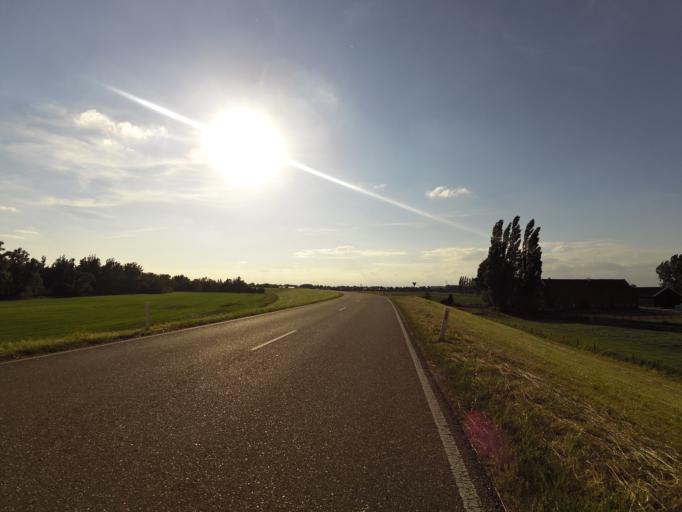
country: NL
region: Gelderland
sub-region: Gemeente Zevenaar
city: Zevenaar
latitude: 51.8843
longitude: 6.0621
